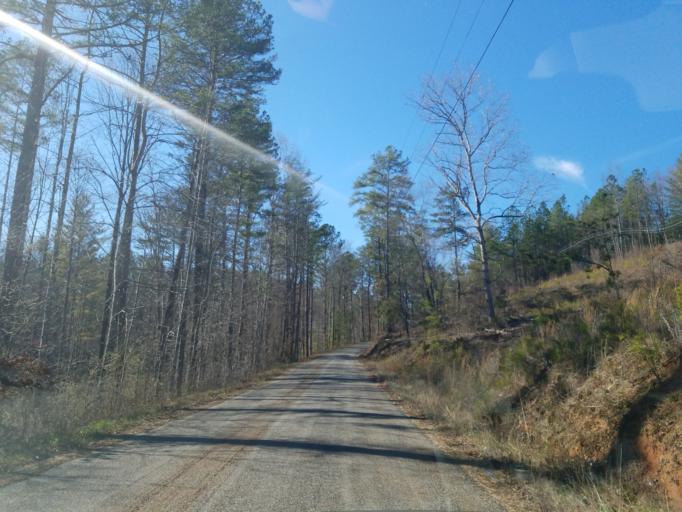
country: US
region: Georgia
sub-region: Dawson County
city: Dawsonville
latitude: 34.5020
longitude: -84.2516
